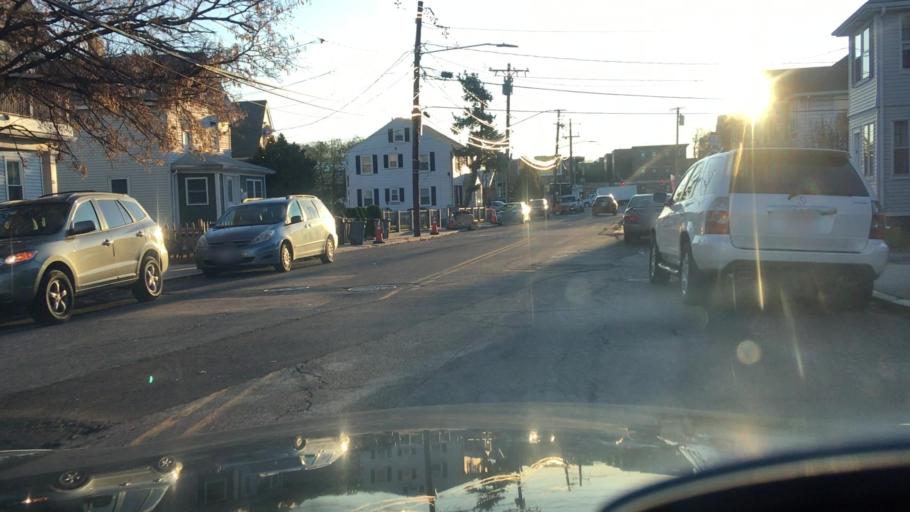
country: US
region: Massachusetts
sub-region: Middlesex County
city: Watertown
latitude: 42.3554
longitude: -71.1516
